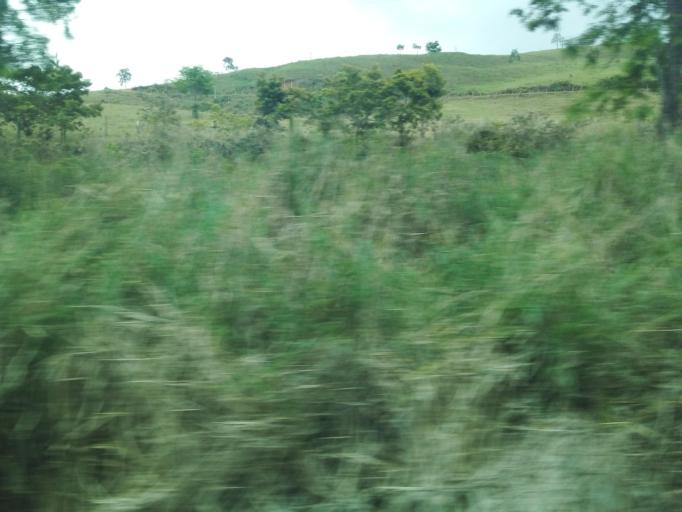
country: BR
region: Minas Gerais
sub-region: Rio Piracicaba
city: Rio Piracicaba
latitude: -19.9731
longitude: -43.2187
